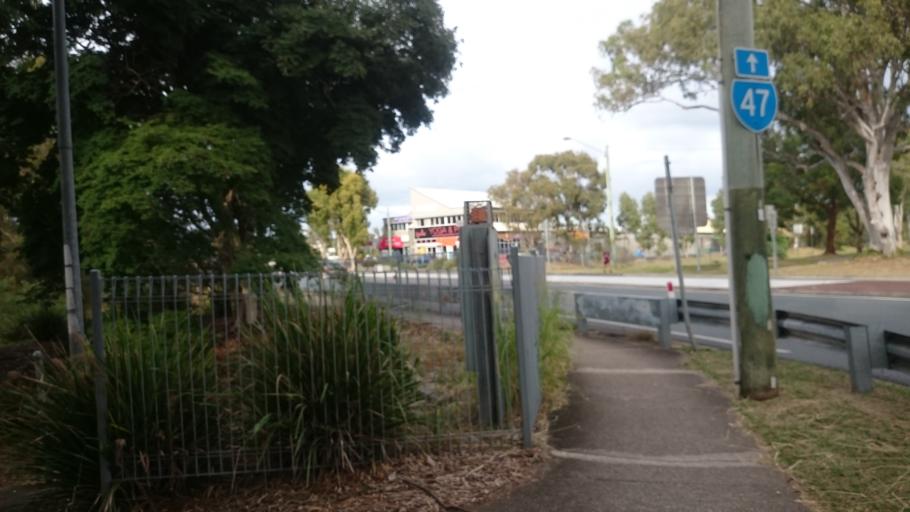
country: AU
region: Queensland
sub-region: Redland
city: Cleveland
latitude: -27.5302
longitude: 153.2670
